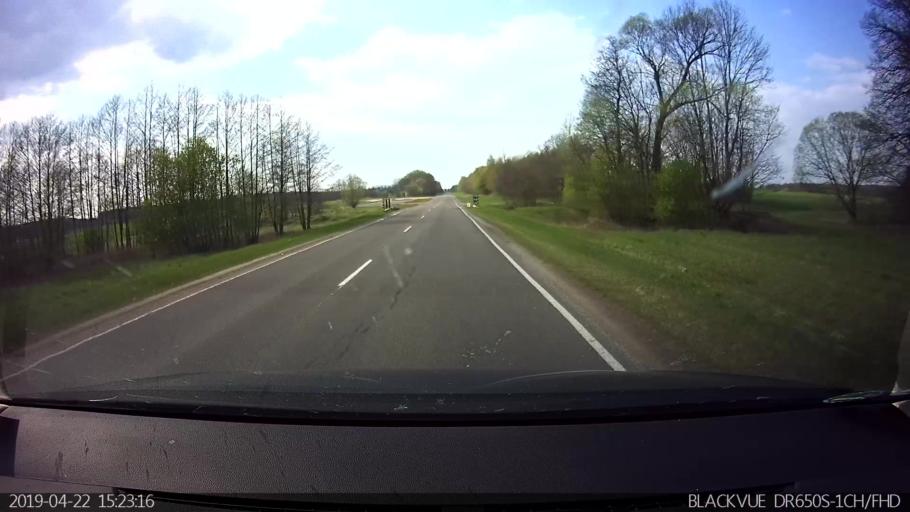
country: BY
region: Brest
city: Vysokaye
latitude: 52.3541
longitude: 23.4300
